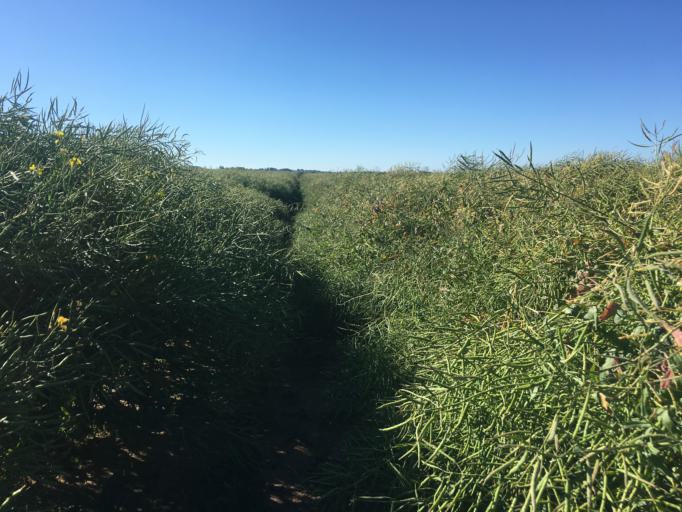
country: GB
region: England
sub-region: Northumberland
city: Beadnell
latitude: 55.5607
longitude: -1.6430
